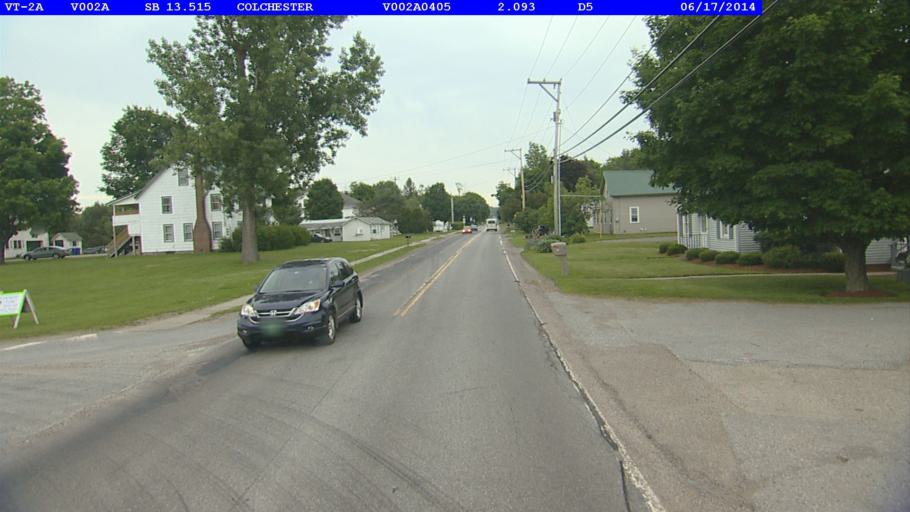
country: US
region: Vermont
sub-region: Chittenden County
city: Colchester
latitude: 44.5480
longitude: -73.1591
